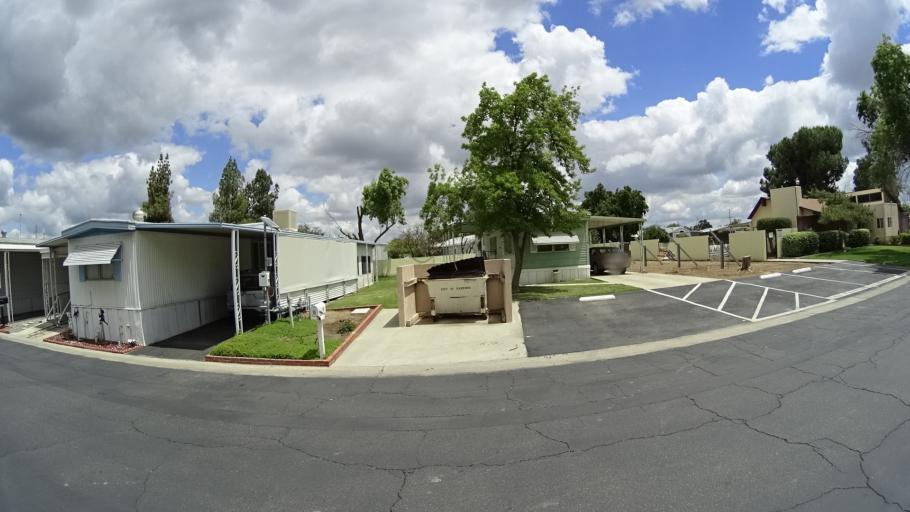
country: US
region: California
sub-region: Kings County
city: Hanford
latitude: 36.3435
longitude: -119.6335
